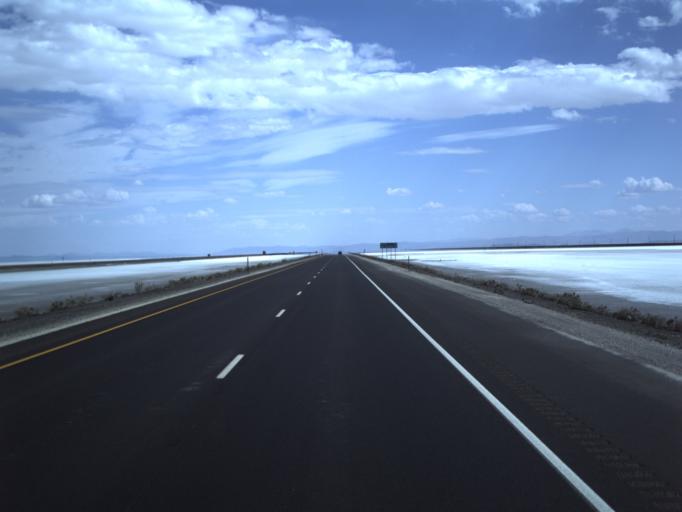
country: US
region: Utah
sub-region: Tooele County
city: Wendover
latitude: 40.7343
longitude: -113.6502
